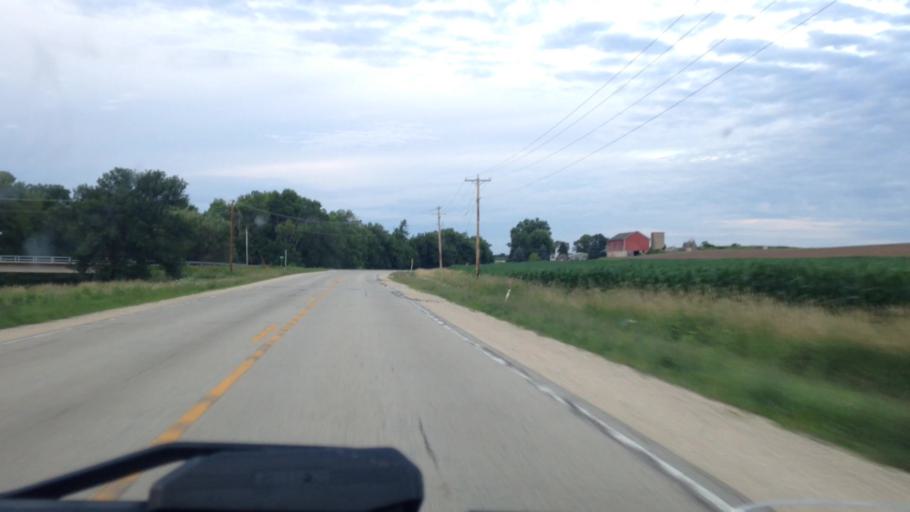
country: US
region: Wisconsin
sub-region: Dodge County
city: Mayville
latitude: 43.4916
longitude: -88.4948
